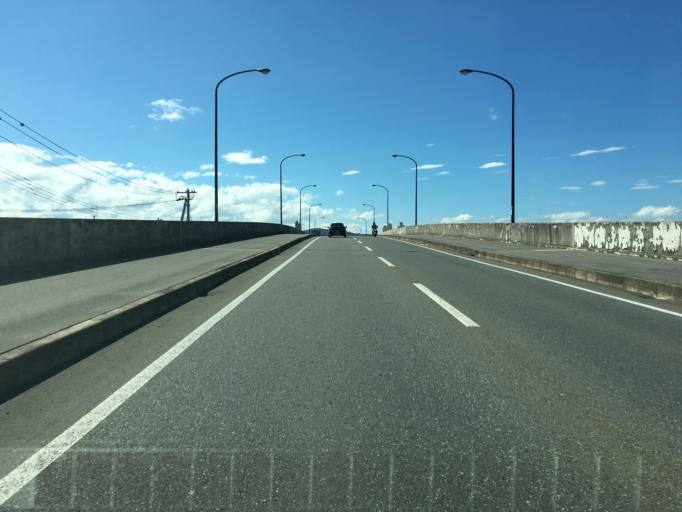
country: JP
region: Yamagata
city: Yonezawa
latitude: 37.9195
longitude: 140.1262
